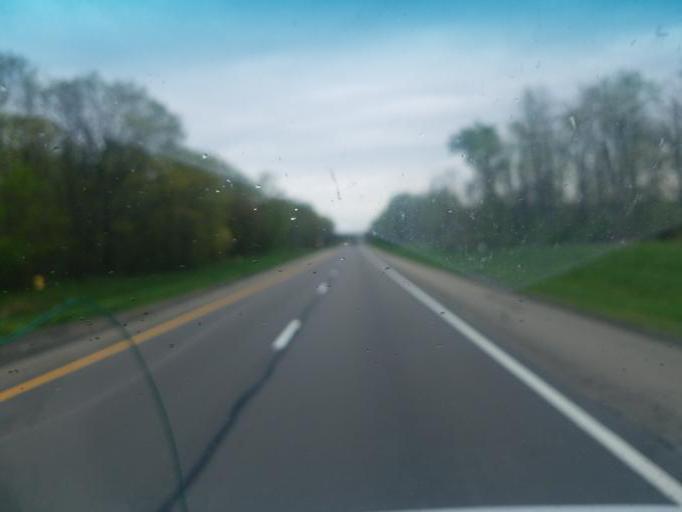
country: US
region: New York
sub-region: Chautauqua County
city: Westfield
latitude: 42.3618
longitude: -79.5255
